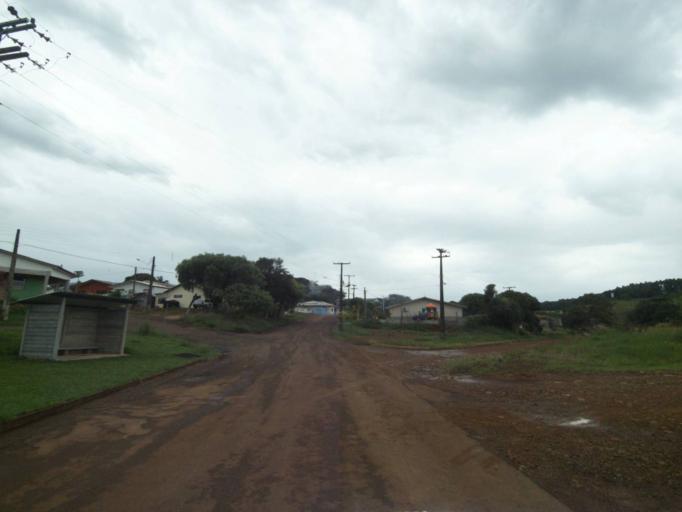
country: BR
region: Parana
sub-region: Guaraniacu
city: Guaraniacu
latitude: -25.1120
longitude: -52.8525
